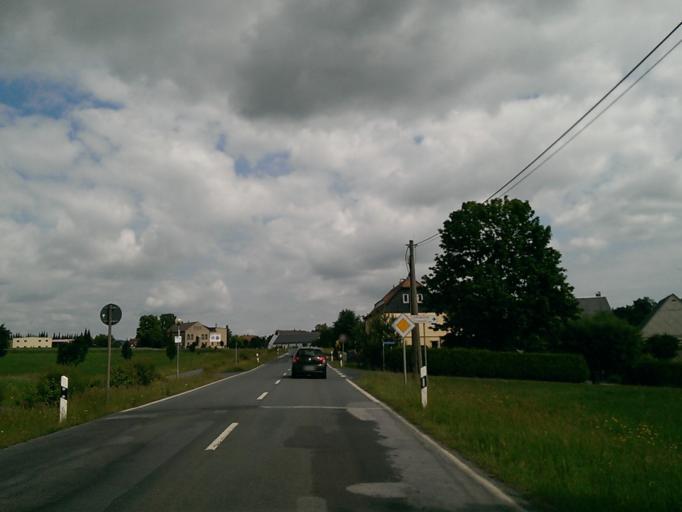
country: DE
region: Saxony
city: Mittelherwigsdorf
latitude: 50.9398
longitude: 14.7449
